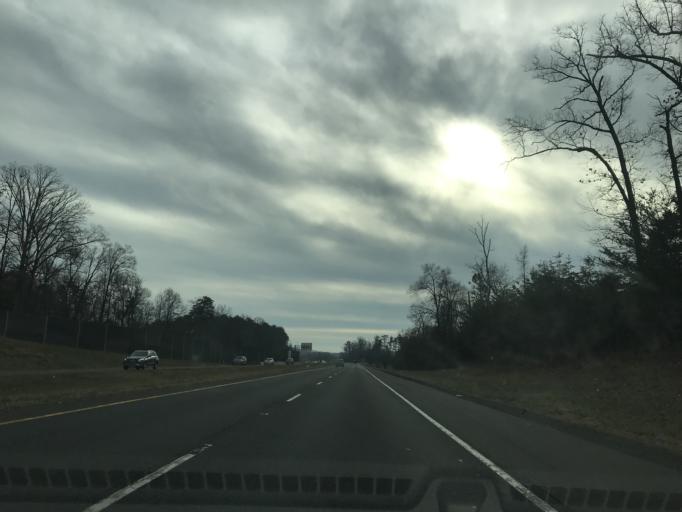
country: US
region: Virginia
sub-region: City of Manassas
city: Manassas
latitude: 38.7291
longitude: -77.5046
